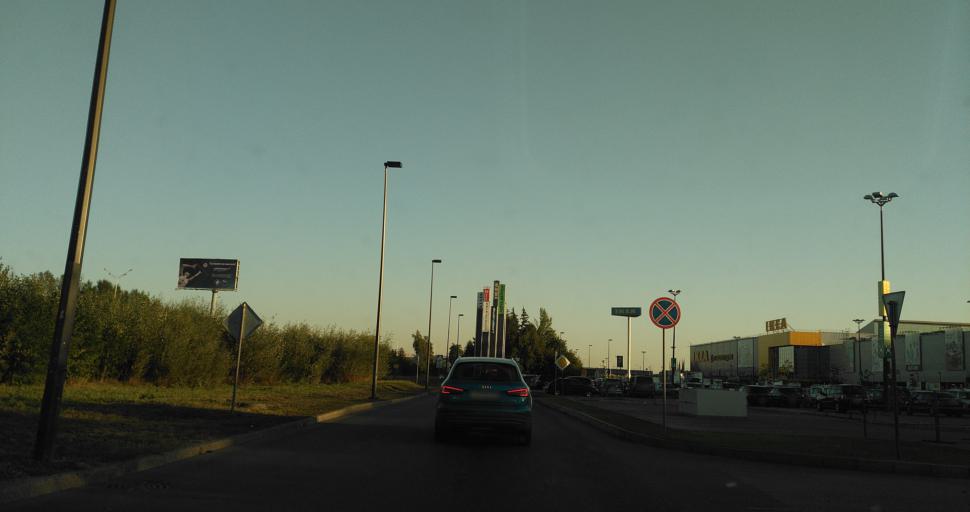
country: RU
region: Bashkortostan
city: Ufa
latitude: 54.6758
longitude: 55.9323
